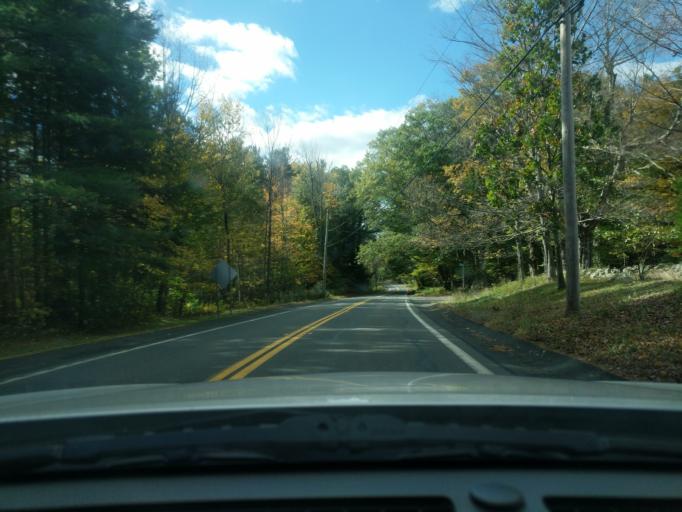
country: US
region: Massachusetts
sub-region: Berkshire County
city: Otis
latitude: 42.1749
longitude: -72.9664
